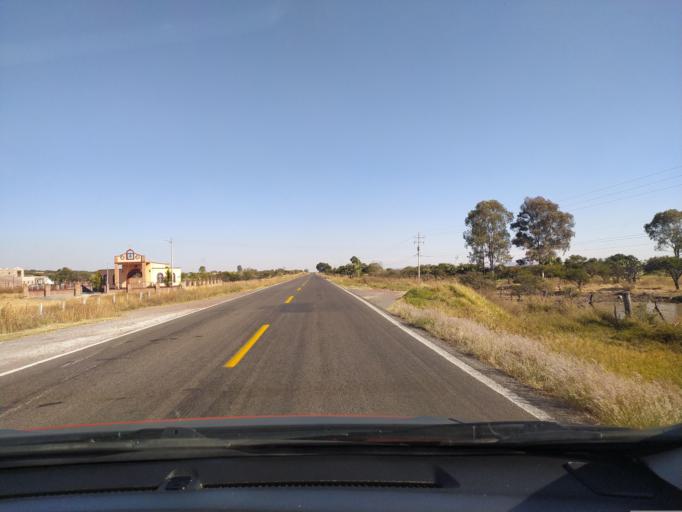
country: MX
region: Jalisco
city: Valle de Guadalupe
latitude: 21.0220
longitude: -102.5389
